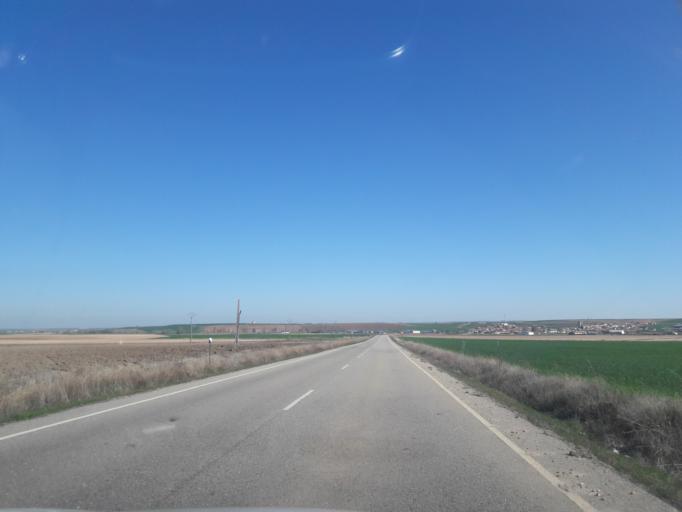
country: ES
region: Castille and Leon
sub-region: Provincia de Salamanca
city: Mancera de Abajo
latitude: 40.8271
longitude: -5.2080
